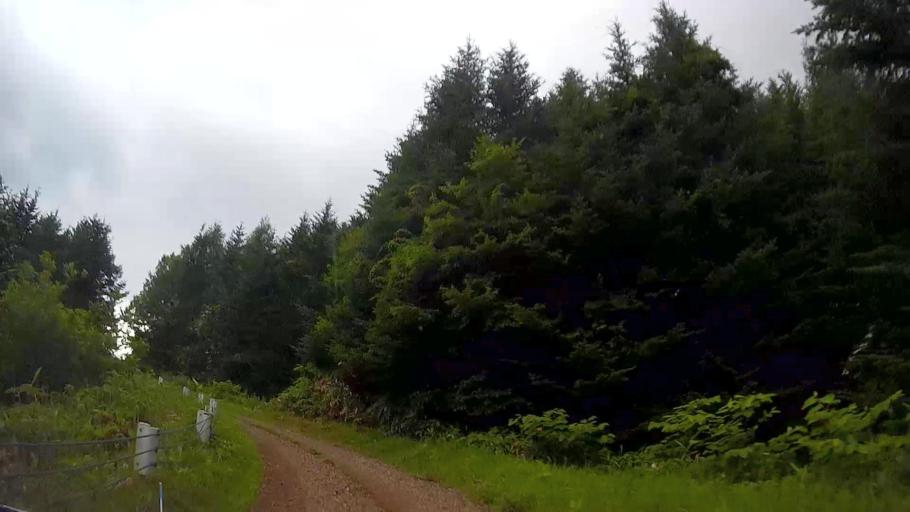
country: JP
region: Hokkaido
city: Nanae
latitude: 42.1256
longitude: 140.4185
